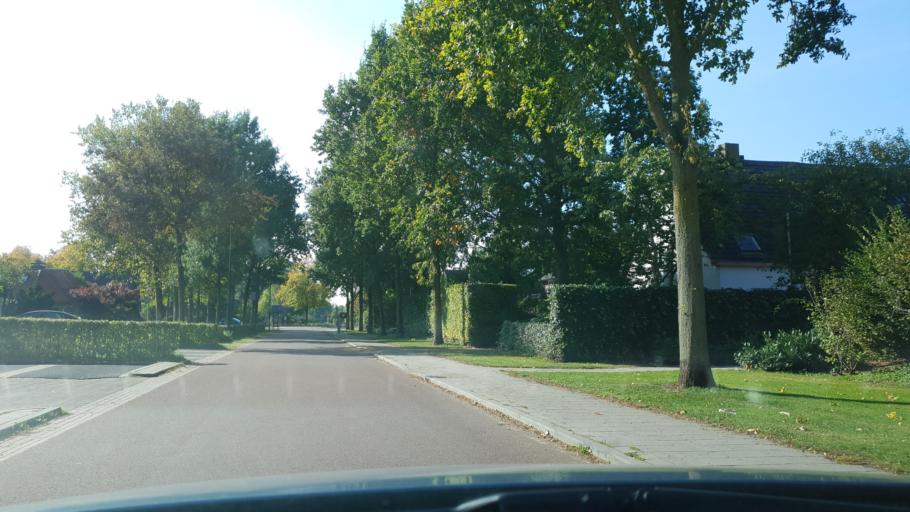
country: NL
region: Gelderland
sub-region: Gemeente Beuningen
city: Beuningen
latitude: 51.8604
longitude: 5.7622
